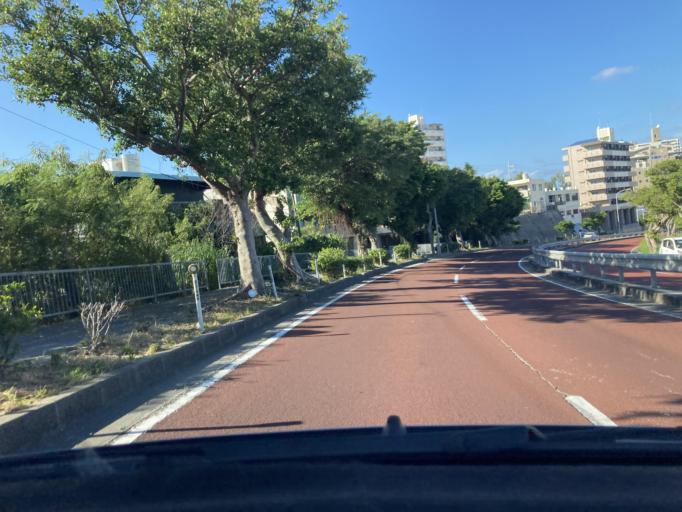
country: JP
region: Okinawa
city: Ginowan
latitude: 26.2608
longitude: 127.7263
